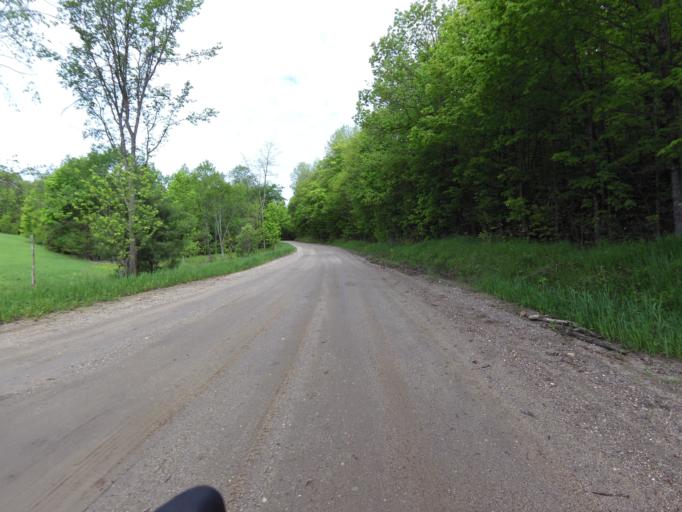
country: CA
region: Quebec
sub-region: Outaouais
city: Wakefield
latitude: 45.7547
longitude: -75.9030
